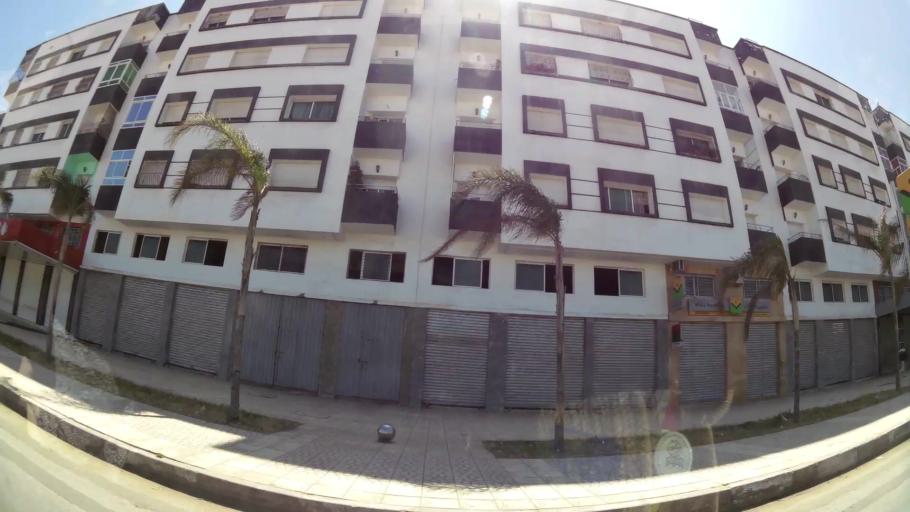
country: MA
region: Gharb-Chrarda-Beni Hssen
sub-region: Kenitra Province
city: Kenitra
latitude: 34.2403
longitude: -6.5476
